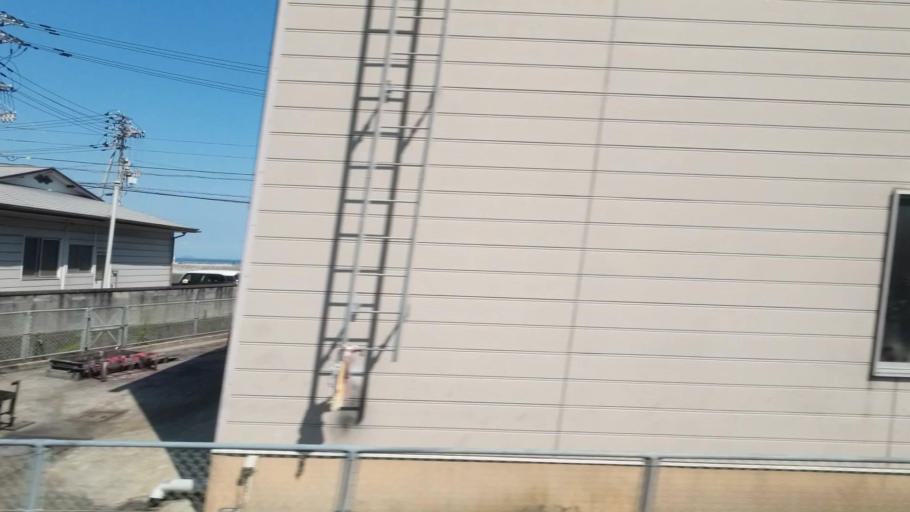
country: JP
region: Ehime
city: Kawanoecho
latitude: 34.0334
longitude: 133.5914
